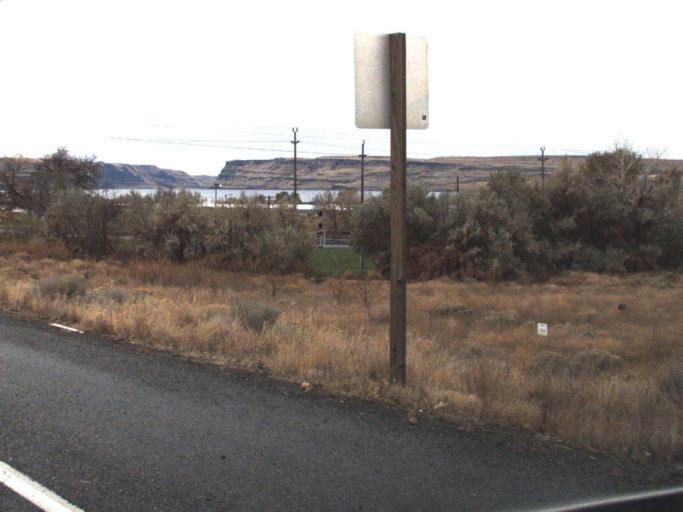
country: US
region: Washington
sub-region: Benton County
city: Finley
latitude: 46.1026
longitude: -118.9130
